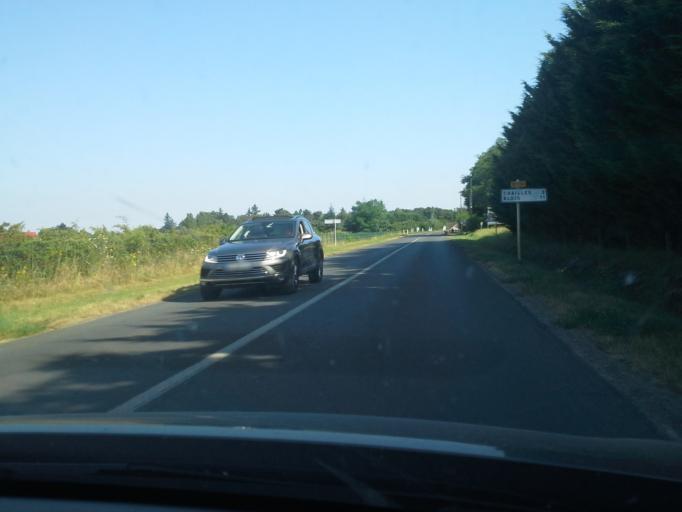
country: FR
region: Centre
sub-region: Departement du Loir-et-Cher
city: Les Montils
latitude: 47.5141
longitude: 1.3003
